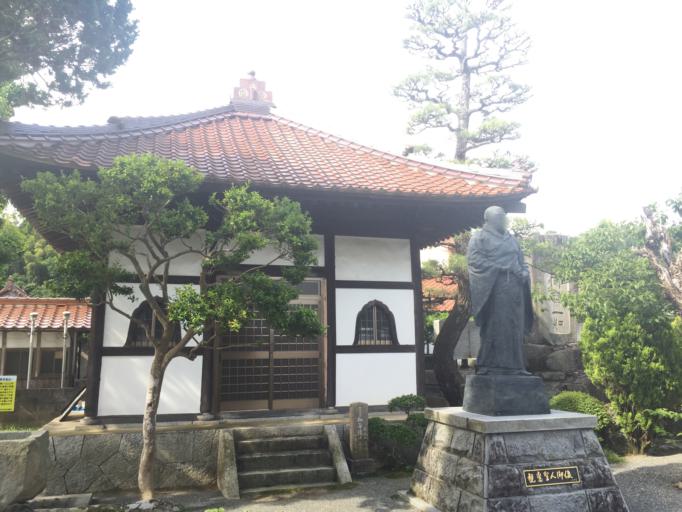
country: JP
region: Hiroshima
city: Takehara
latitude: 34.4450
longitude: 132.7884
